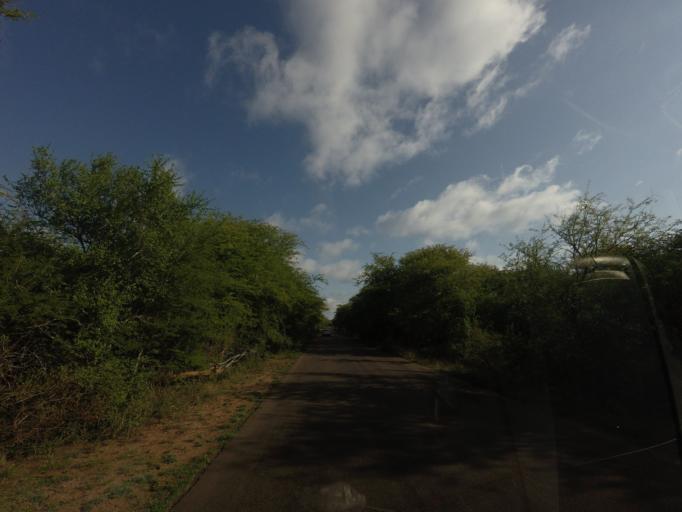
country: ZA
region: Mpumalanga
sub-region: Ehlanzeni District
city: Komatipoort
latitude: -25.2375
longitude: 31.8504
